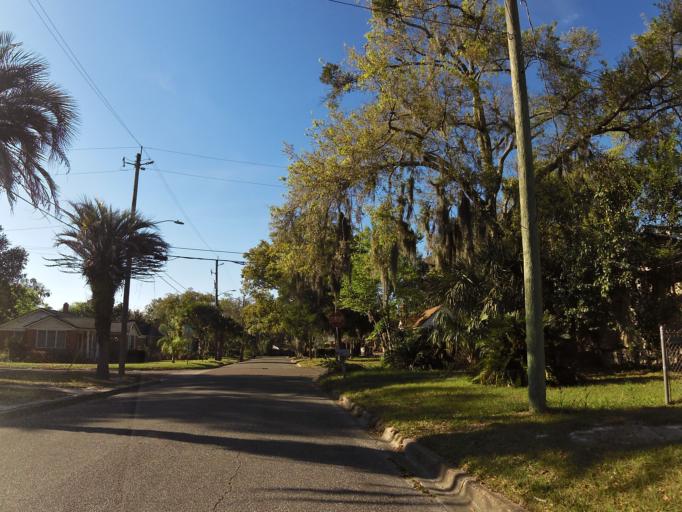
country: US
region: Florida
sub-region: Duval County
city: Jacksonville
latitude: 30.3856
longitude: -81.6545
